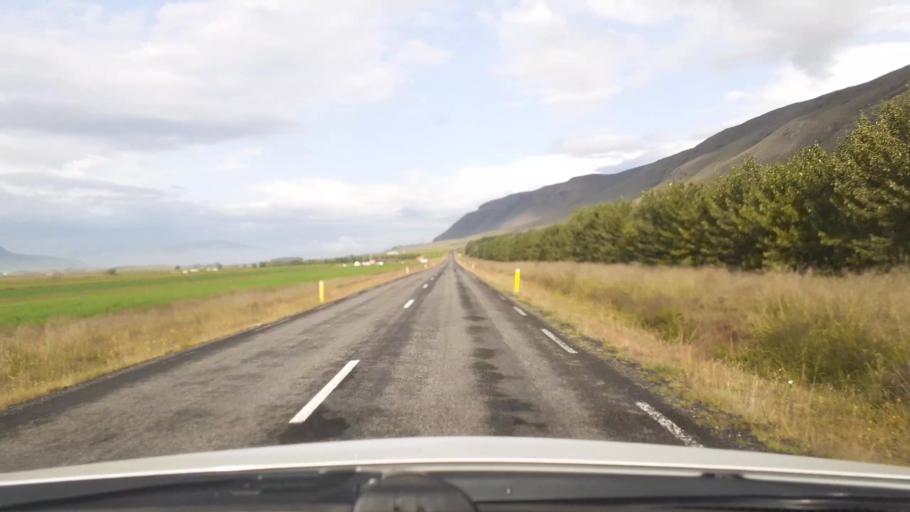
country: IS
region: Capital Region
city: Mosfellsbaer
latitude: 64.3386
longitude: -21.5381
